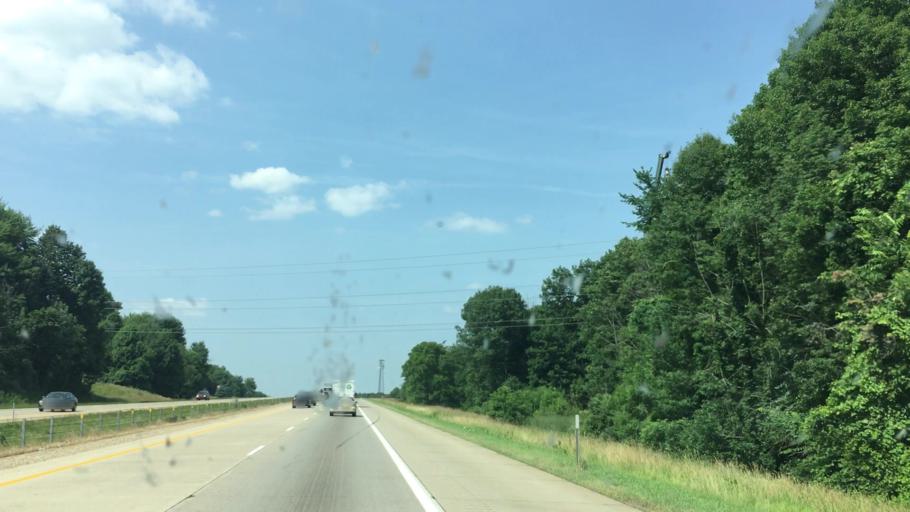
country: US
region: Michigan
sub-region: Allegan County
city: Plainwell
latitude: 42.4846
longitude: -85.6521
